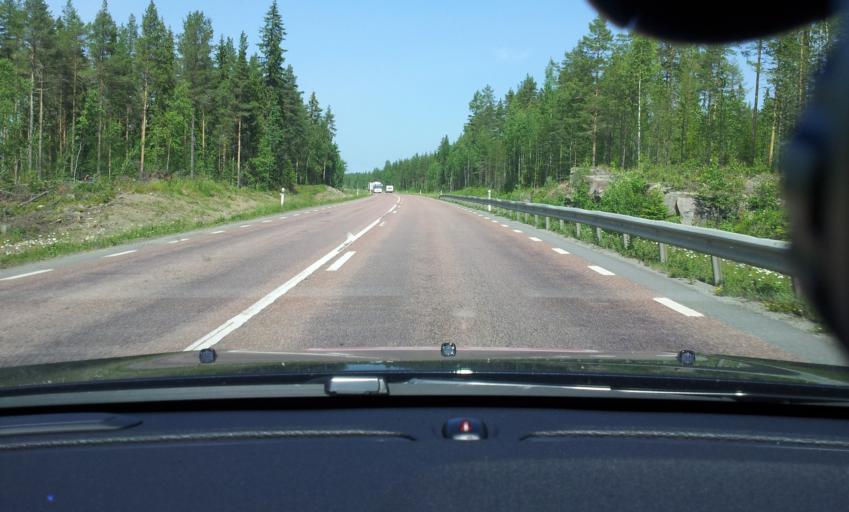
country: SE
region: Jaemtland
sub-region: Bergs Kommun
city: Hoverberg
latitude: 62.8074
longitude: 14.5177
